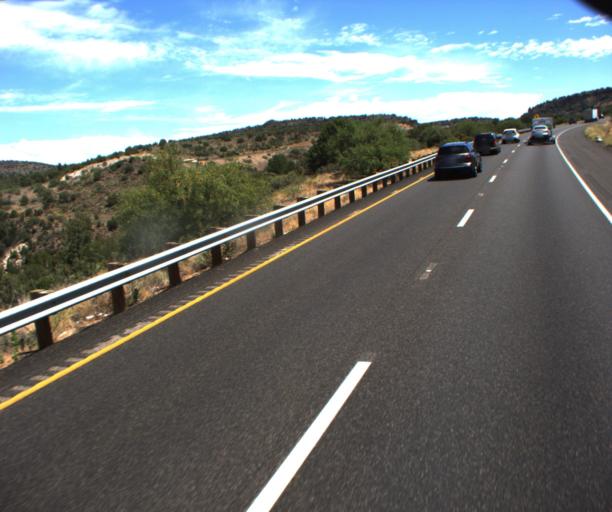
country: US
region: Arizona
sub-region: Yavapai County
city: Big Park
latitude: 34.7059
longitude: -111.7364
